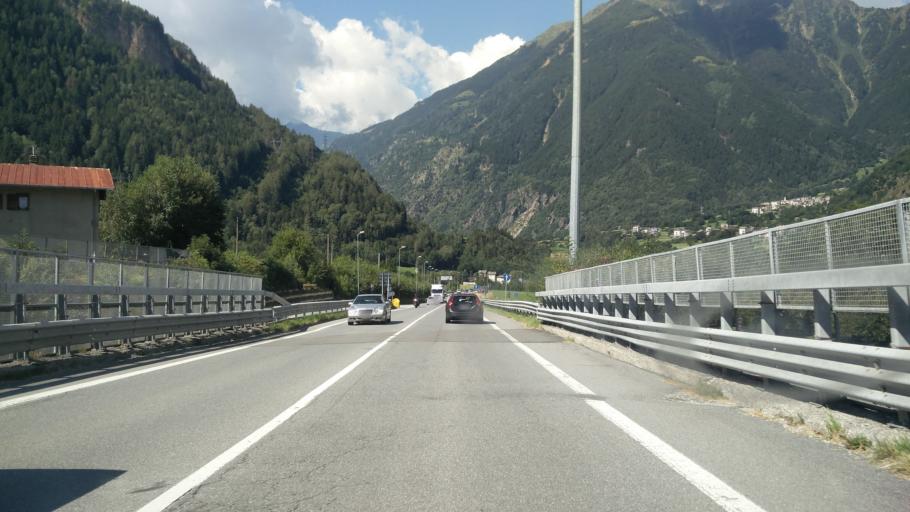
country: IT
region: Lombardy
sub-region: Provincia di Sondrio
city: Sondalo
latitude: 46.3256
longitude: 10.3359
